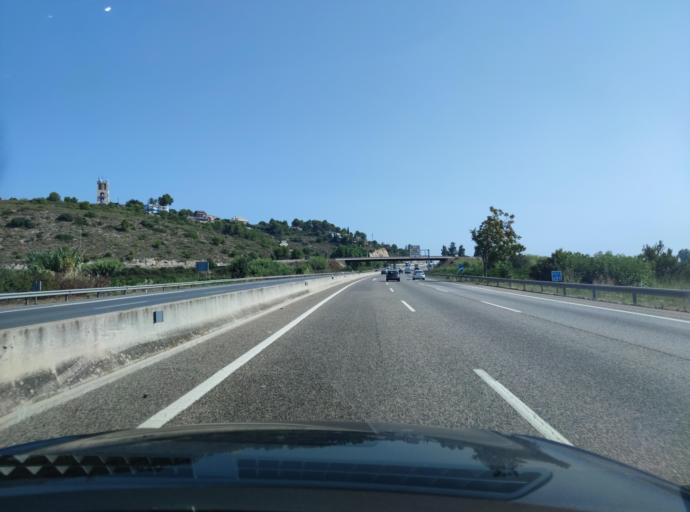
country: ES
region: Valencia
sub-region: Provincia de Valencia
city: Gavarda
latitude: 39.0842
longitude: -0.5403
